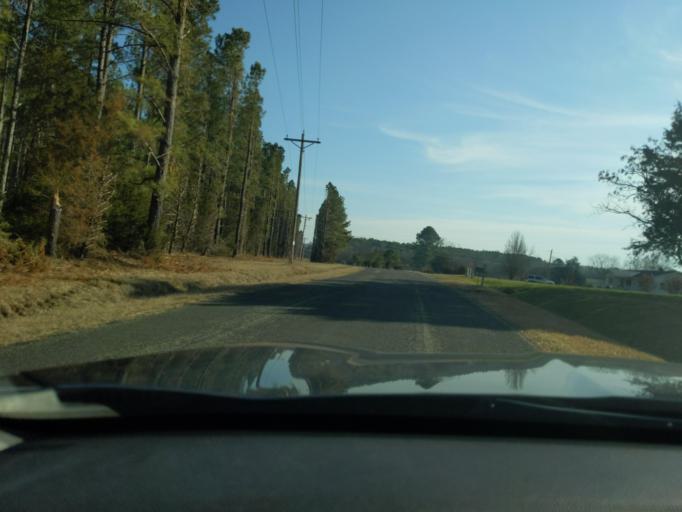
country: US
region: South Carolina
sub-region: Abbeville County
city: Calhoun Falls
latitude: 34.0812
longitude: -82.5694
